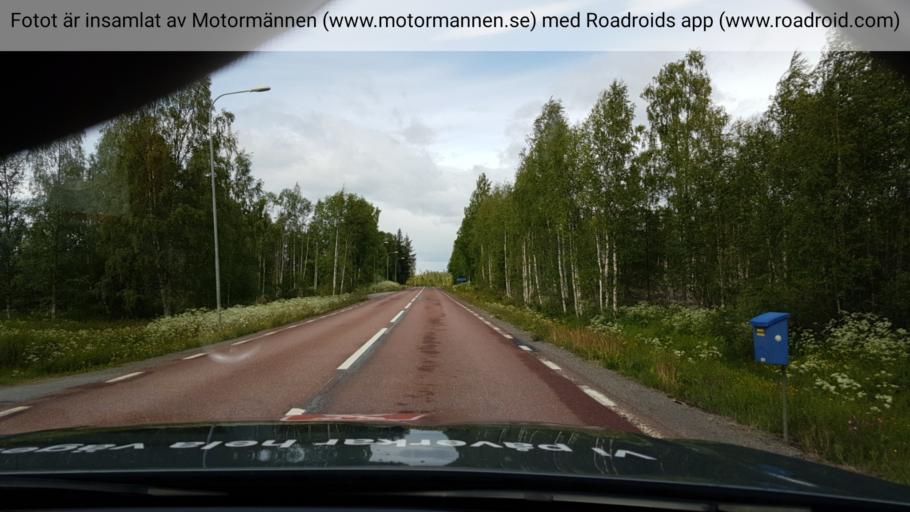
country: SE
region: Vaesterbotten
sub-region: Dorotea Kommun
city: Dorotea
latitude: 64.0406
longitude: 16.0208
